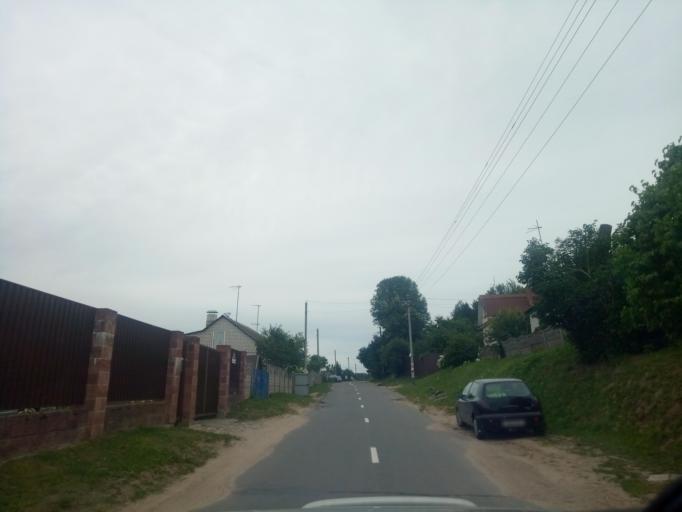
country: BY
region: Minsk
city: Zhdanovichy
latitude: 53.9276
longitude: 27.3836
